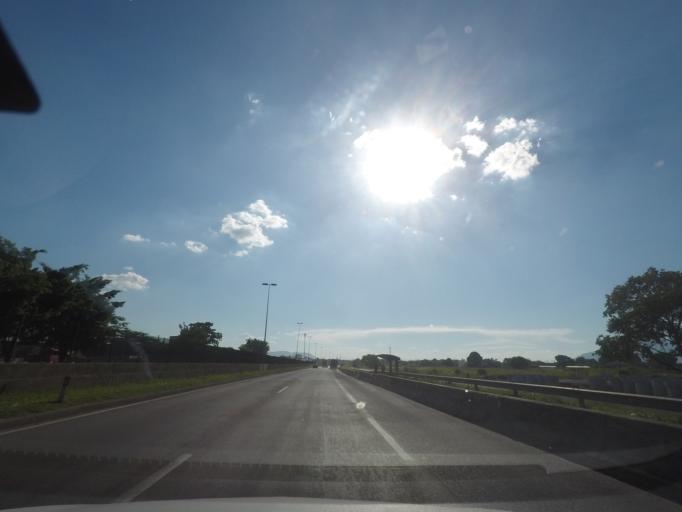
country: BR
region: Rio de Janeiro
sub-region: Duque De Caxias
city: Duque de Caxias
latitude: -22.6658
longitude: -43.2616
